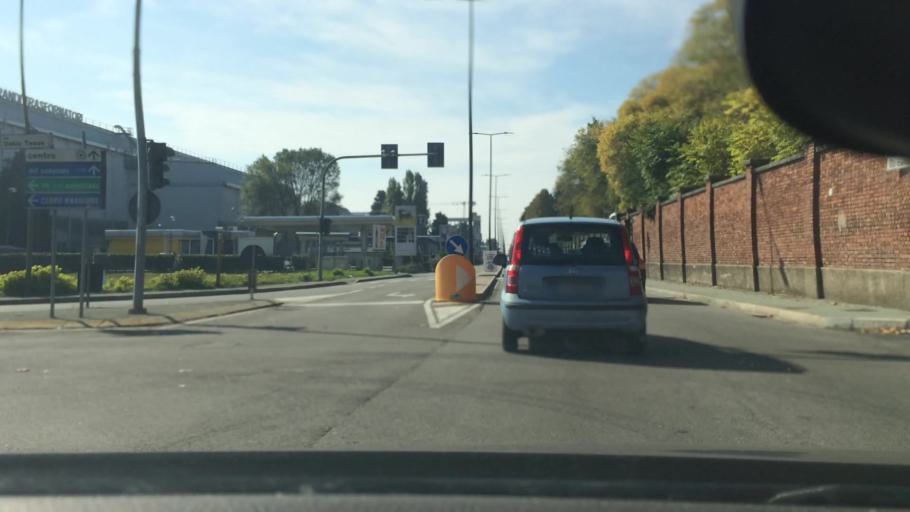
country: IT
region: Lombardy
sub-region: Citta metropolitana di Milano
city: San Vittore Olona
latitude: 45.5995
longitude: 8.9405
